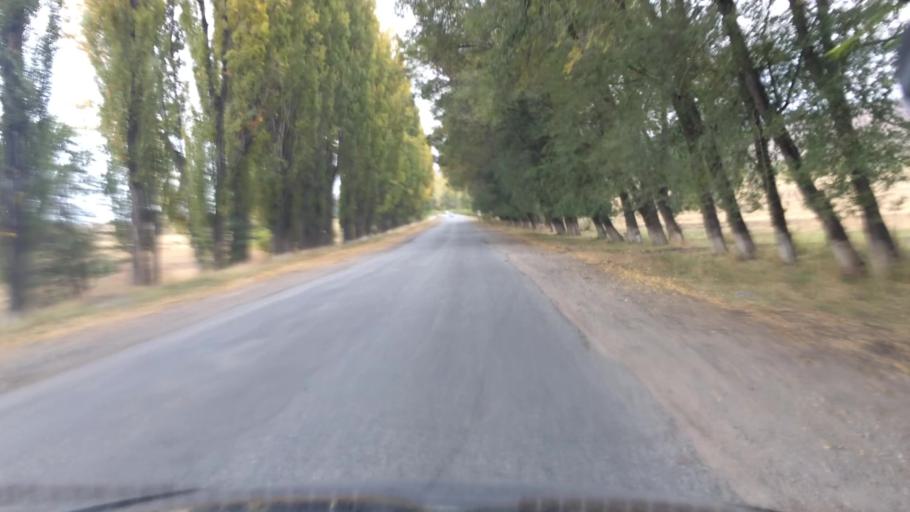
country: KG
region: Ysyk-Koel
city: Pokrovka
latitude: 42.7392
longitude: 77.9103
